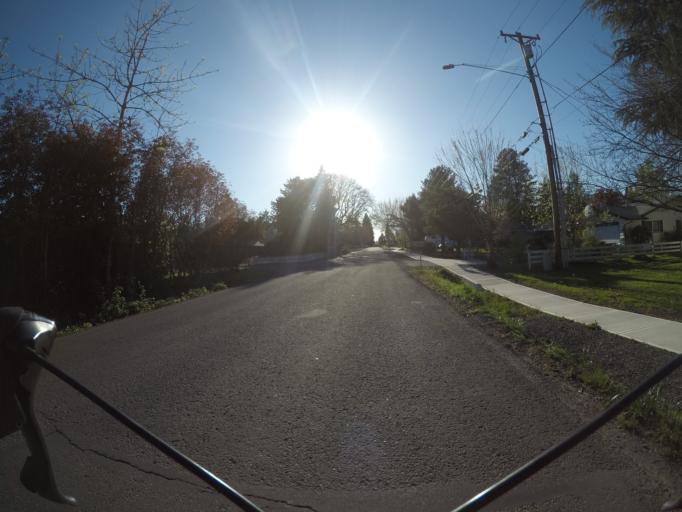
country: US
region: Oregon
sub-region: Washington County
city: Aloha
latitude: 45.4787
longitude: -122.8695
